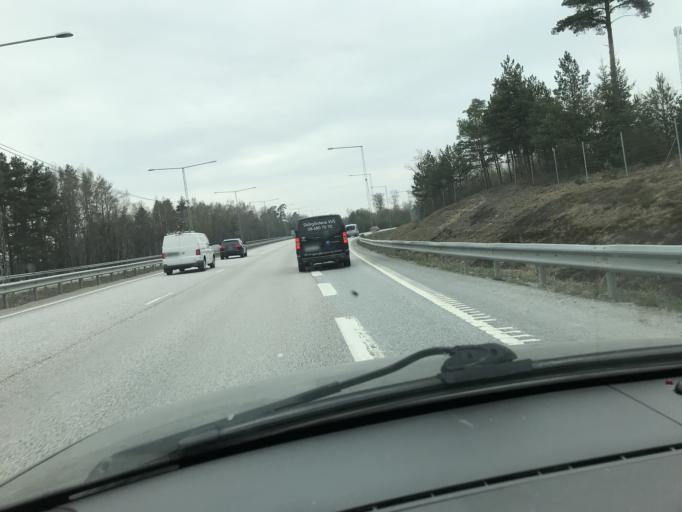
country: SE
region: Stockholm
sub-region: Vallentuna Kommun
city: Vallentuna
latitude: 59.4932
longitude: 18.1639
